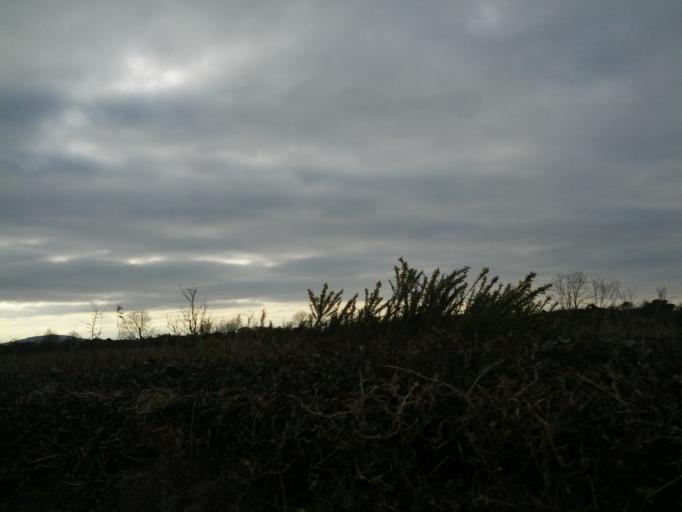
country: IE
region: Connaught
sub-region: County Galway
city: Oranmore
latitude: 53.1917
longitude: -8.9226
